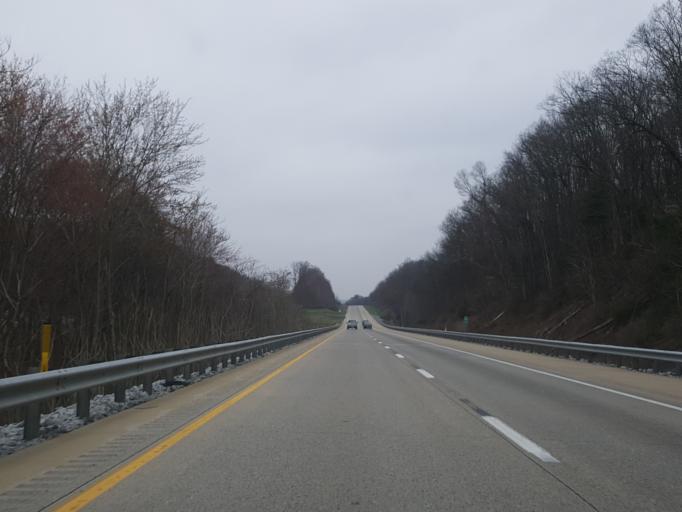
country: US
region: Pennsylvania
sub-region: Lebanon County
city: Jonestown
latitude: 40.4977
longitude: -76.5118
